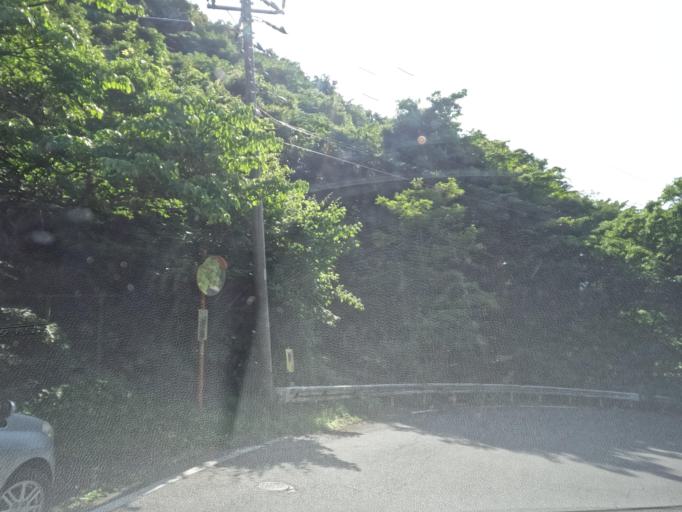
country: JP
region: Saitama
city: Yorii
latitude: 36.0482
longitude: 139.1474
